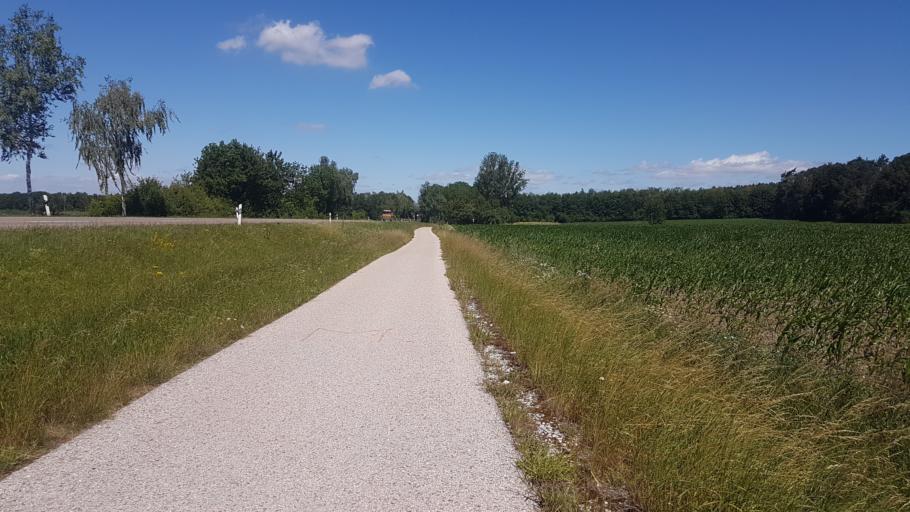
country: DE
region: Bavaria
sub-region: Regierungsbezirk Mittelfranken
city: Herrieden
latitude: 49.2456
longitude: 10.4680
